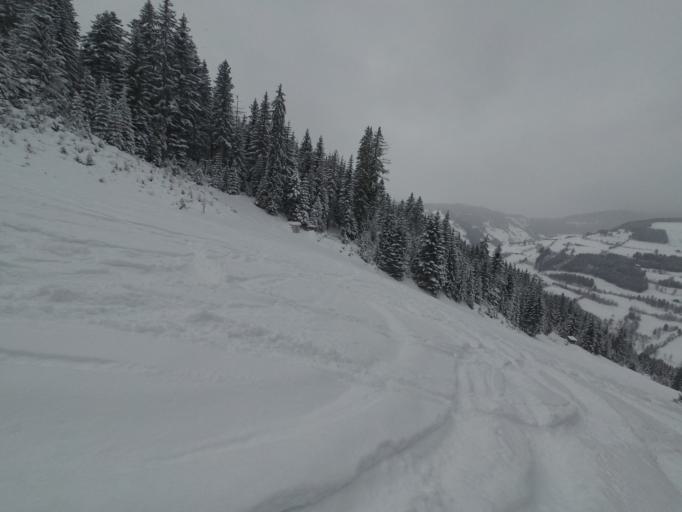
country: AT
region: Salzburg
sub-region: Politischer Bezirk Sankt Johann im Pongau
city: Wagrain
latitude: 47.3248
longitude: 13.2910
